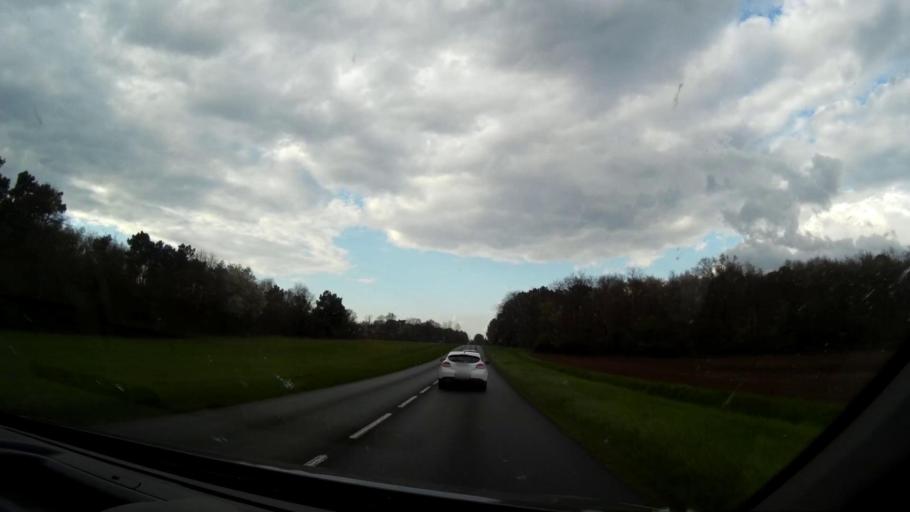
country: FR
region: Centre
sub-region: Departement du Loir-et-Cher
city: Cormeray
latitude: 47.4590
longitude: 1.4253
